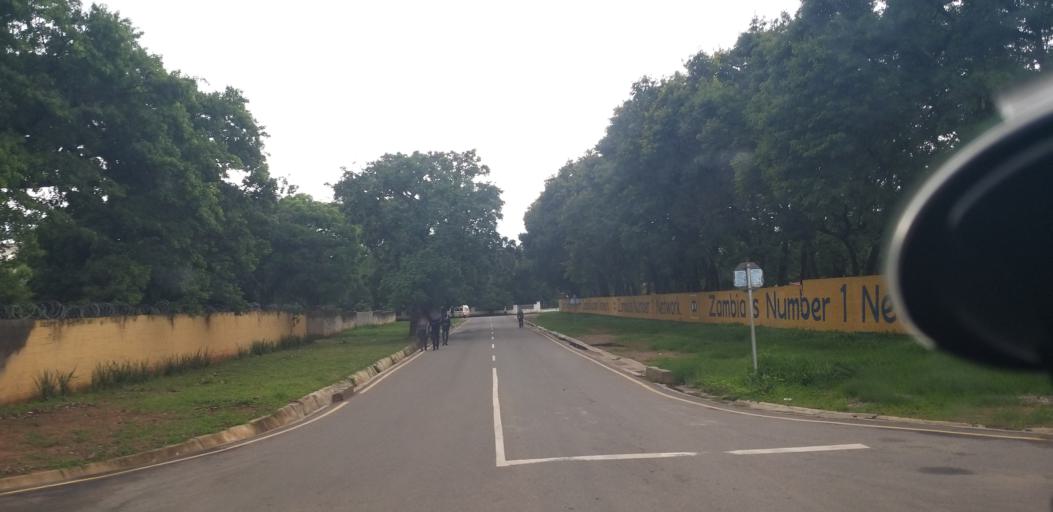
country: ZM
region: Lusaka
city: Lusaka
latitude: -15.4140
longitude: 28.3001
